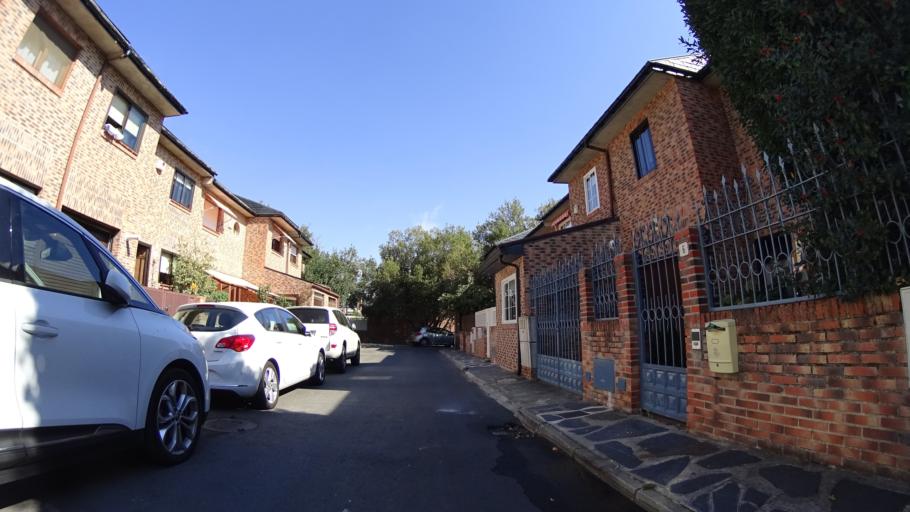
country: ES
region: Madrid
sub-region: Provincia de Madrid
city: Navalquejigo
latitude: 40.6065
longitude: -4.0250
